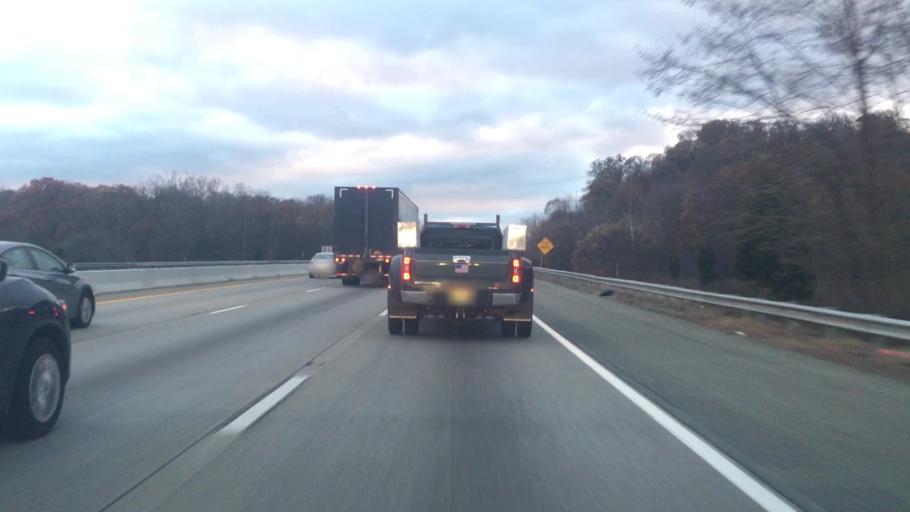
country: US
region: New Jersey
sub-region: Bergen County
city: Oakland
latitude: 41.0242
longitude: -74.2646
